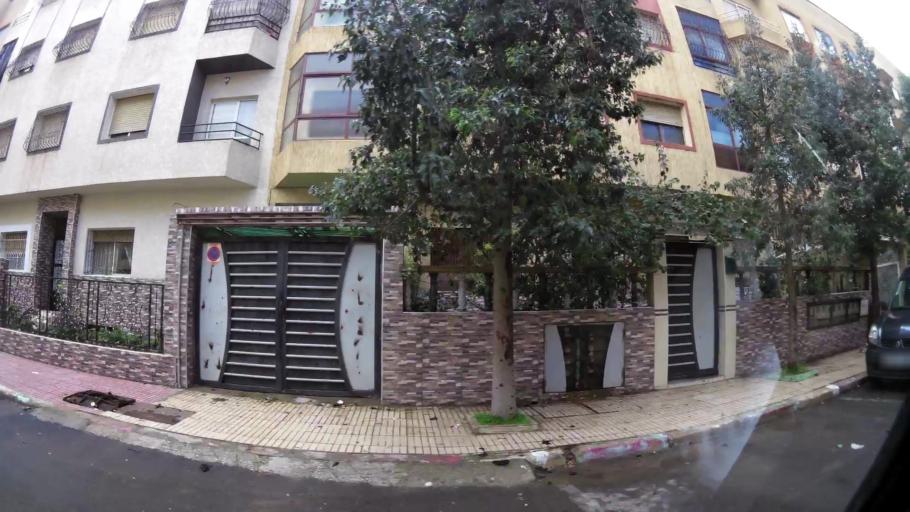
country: MA
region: Grand Casablanca
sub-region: Mediouna
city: Tit Mellil
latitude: 33.5457
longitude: -7.4833
